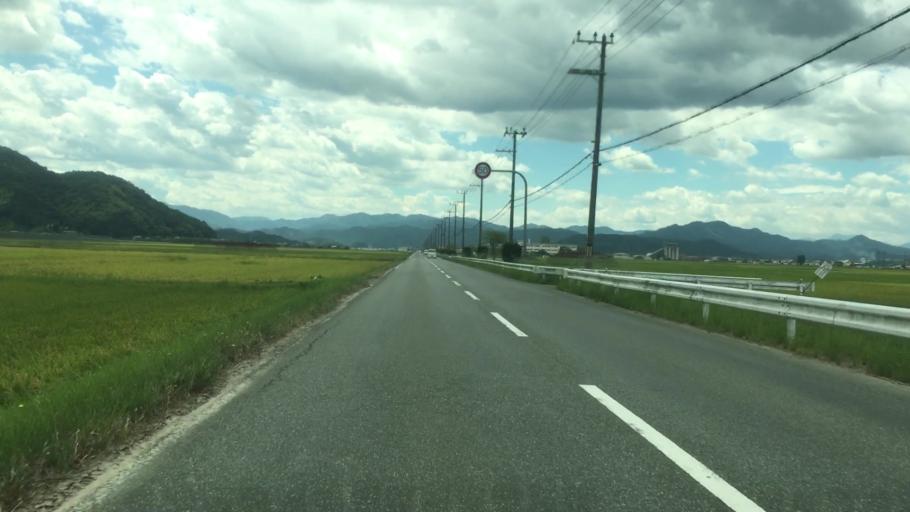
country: JP
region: Hyogo
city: Toyooka
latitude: 35.5395
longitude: 134.8396
